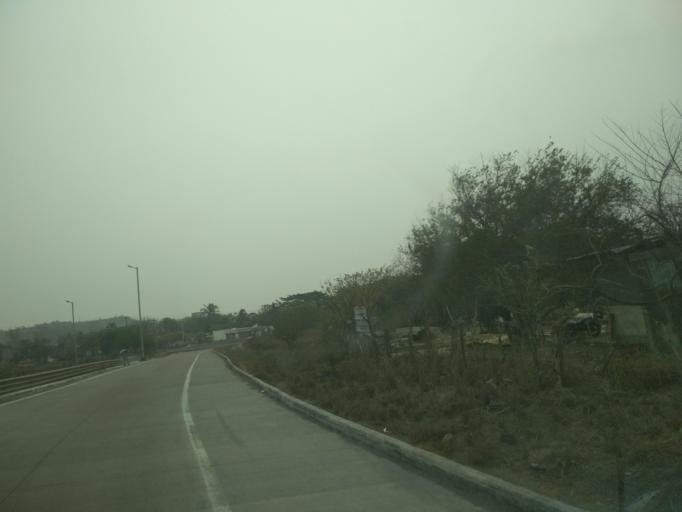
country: MX
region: Veracruz
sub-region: Veracruz
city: Colonia el Renacimiento
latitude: 19.2171
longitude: -96.2203
